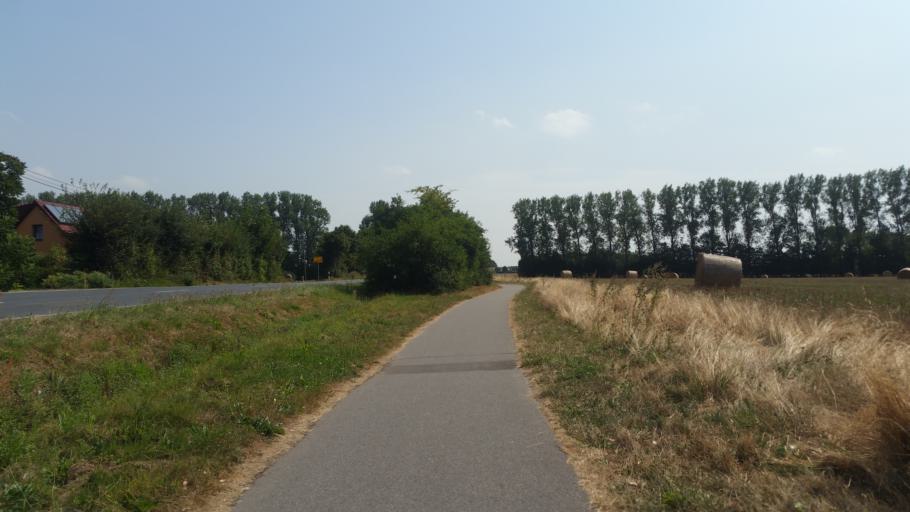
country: DE
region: Mecklenburg-Vorpommern
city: Bastorf
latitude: 54.0980
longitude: 11.6332
